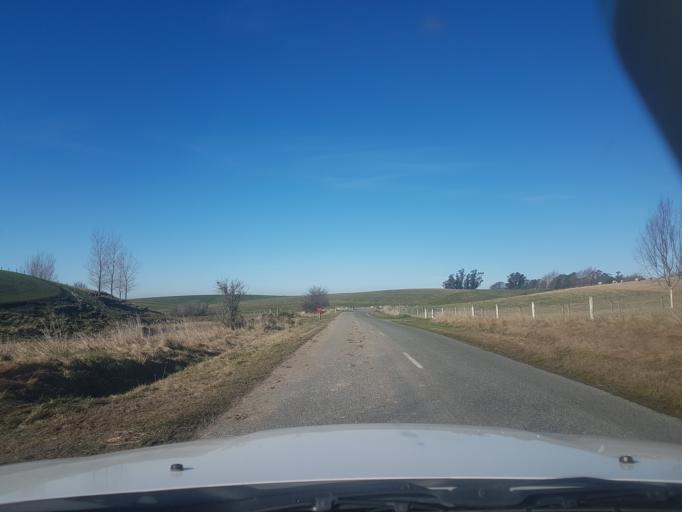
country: NZ
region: Canterbury
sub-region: Timaru District
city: Pleasant Point
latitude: -44.3776
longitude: 171.0869
